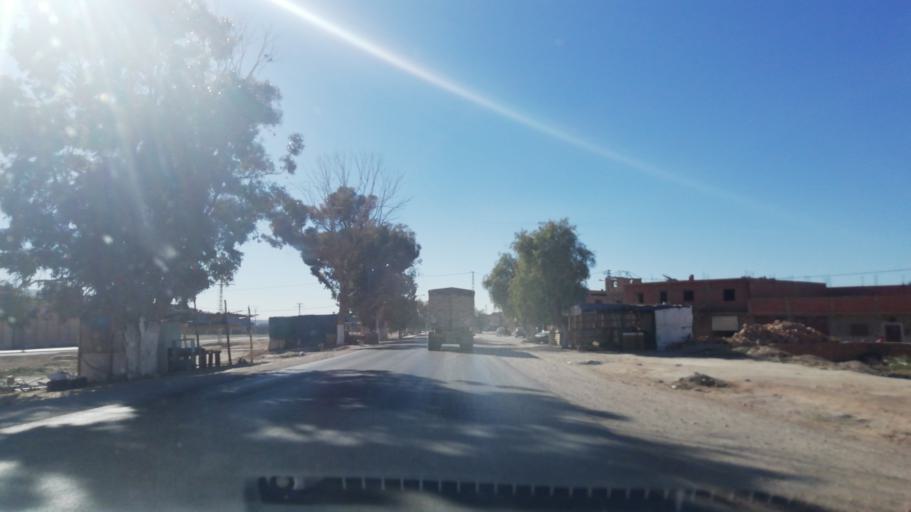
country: DZ
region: Saida
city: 'Ain el Hadjar
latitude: 34.1531
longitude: 0.0701
